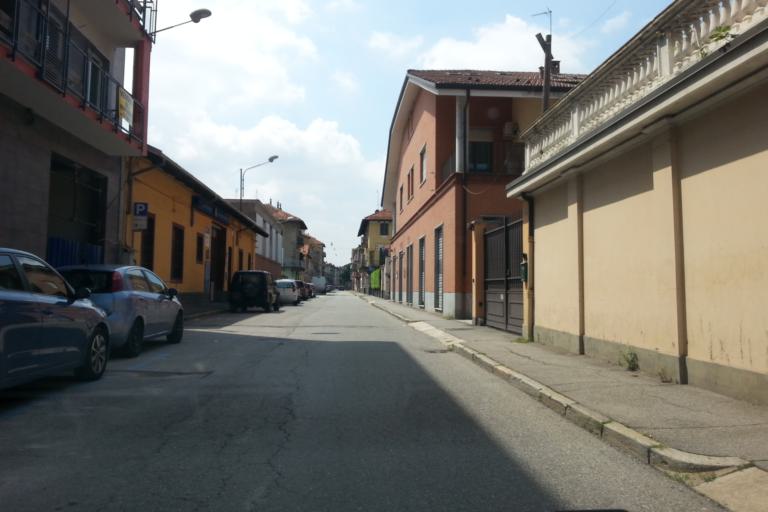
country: IT
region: Piedmont
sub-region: Provincia di Torino
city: Venaria Reale
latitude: 45.1318
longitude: 7.6329
